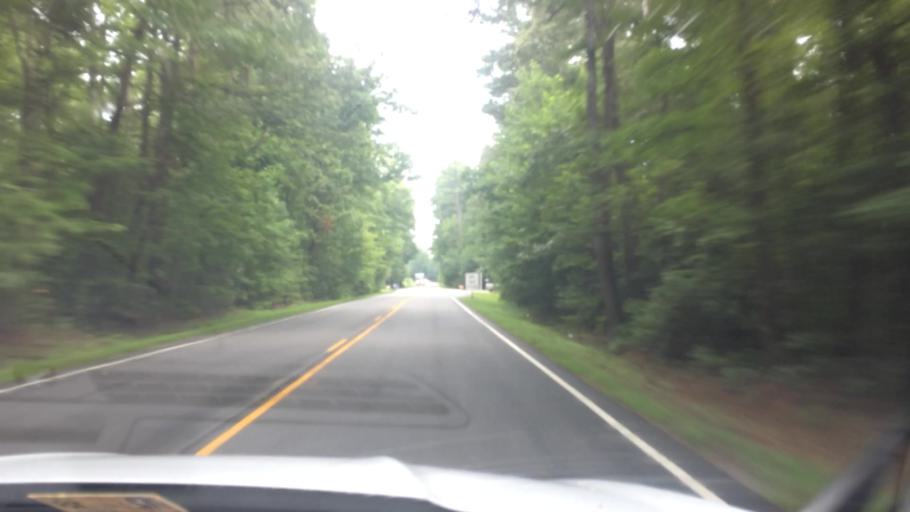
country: US
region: Virginia
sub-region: King William County
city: West Point
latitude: 37.4432
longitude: -76.8379
